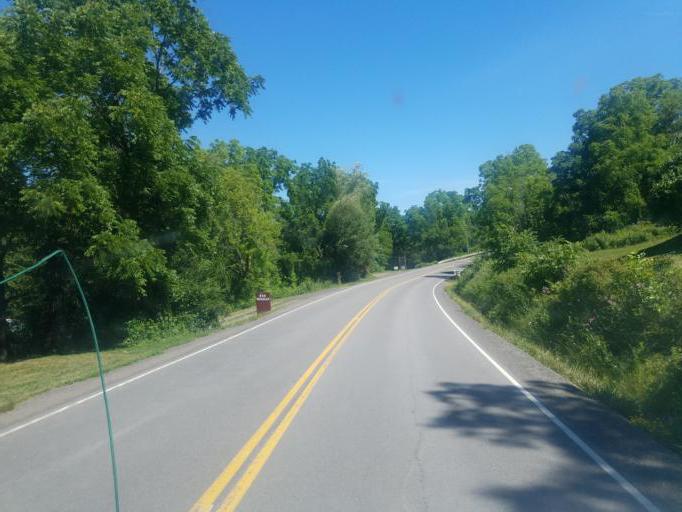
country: US
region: New York
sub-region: Ontario County
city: Naples
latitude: 42.7343
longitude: -77.3250
